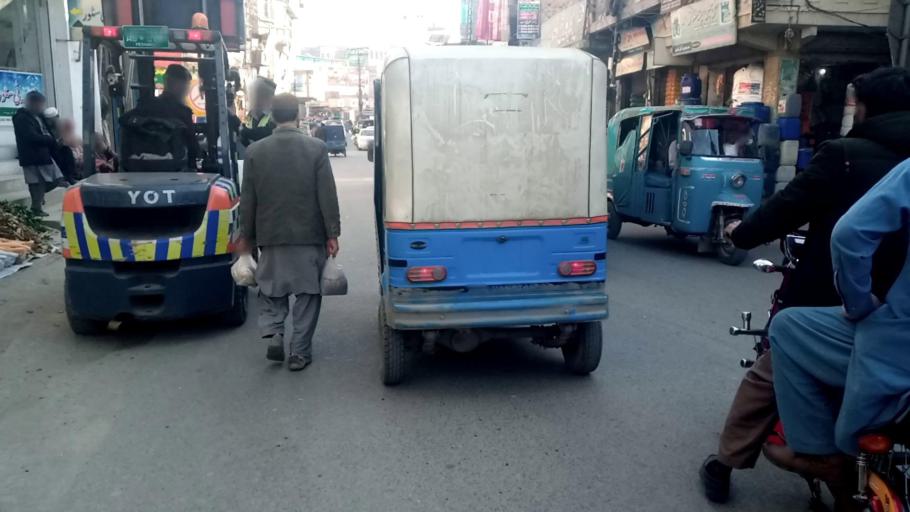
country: PK
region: Khyber Pakhtunkhwa
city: Mingora
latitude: 34.7774
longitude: 72.3575
